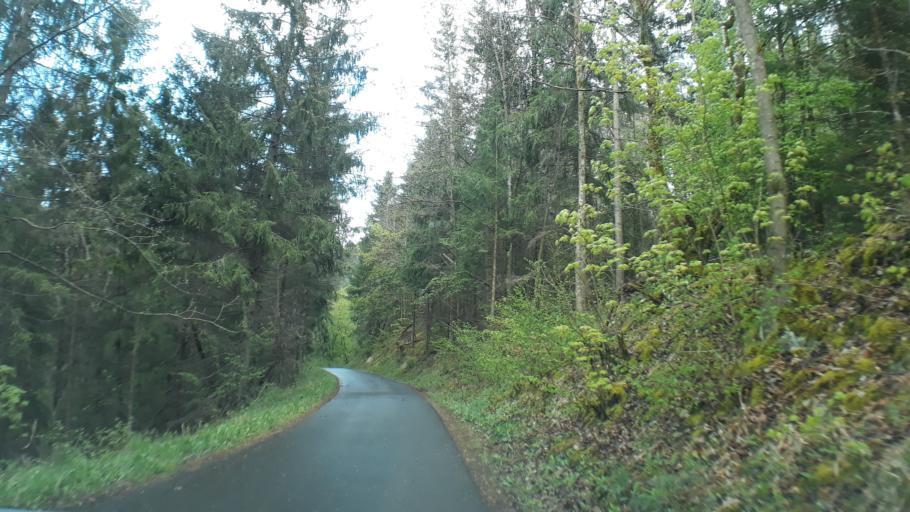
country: DE
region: North Rhine-Westphalia
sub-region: Regierungsbezirk Koln
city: Kall
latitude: 50.5174
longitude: 6.5611
